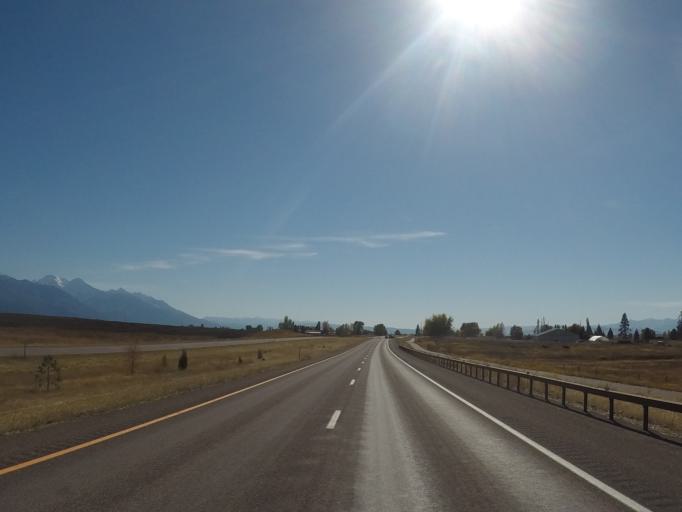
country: US
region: Montana
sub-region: Lake County
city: Pablo
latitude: 47.5754
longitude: -114.1136
